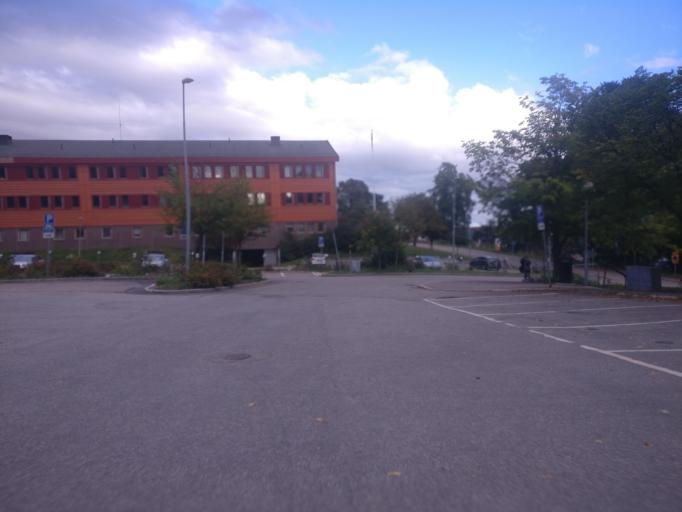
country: SE
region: Vaesternorrland
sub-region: Sundsvalls Kommun
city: Sundsvall
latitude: 62.3953
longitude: 17.3100
